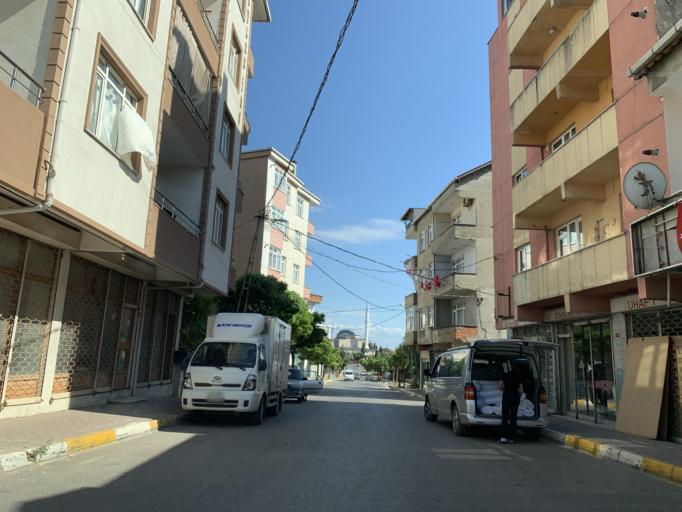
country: TR
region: Istanbul
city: Pendik
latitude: 40.8835
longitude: 29.2797
